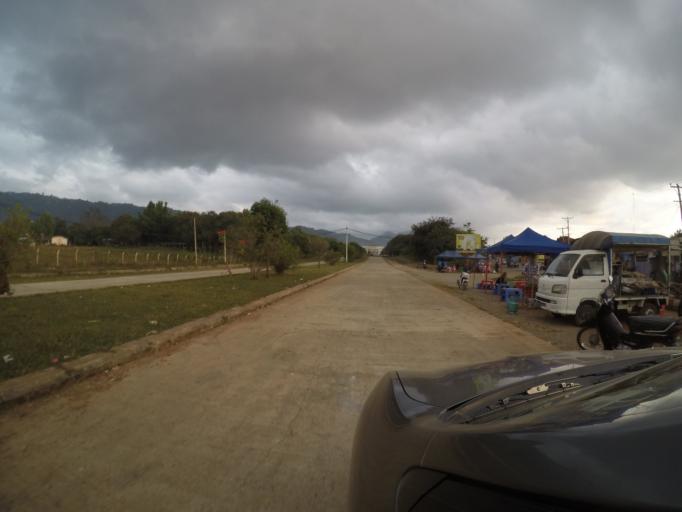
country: MM
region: Shan
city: Taunggyi
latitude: 20.7695
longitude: 97.0011
